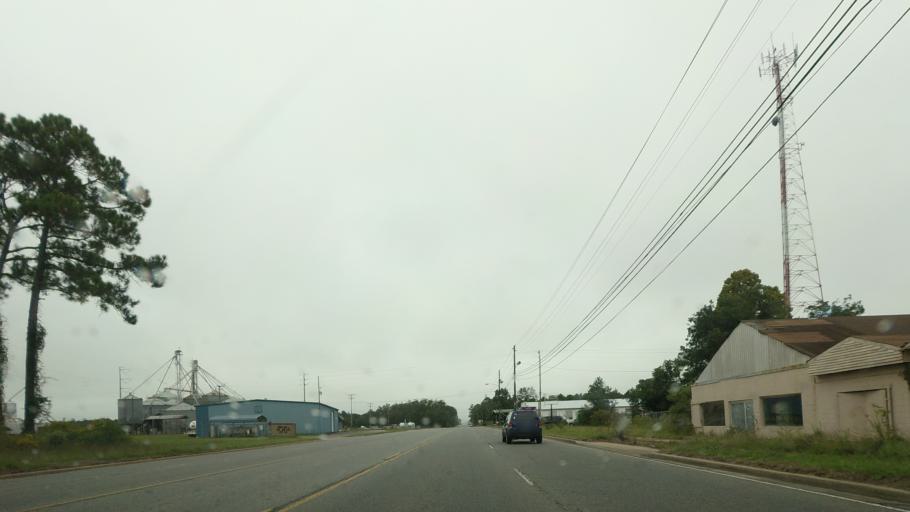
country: US
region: Georgia
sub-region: Irwin County
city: Ocilla
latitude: 31.6066
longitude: -83.2501
